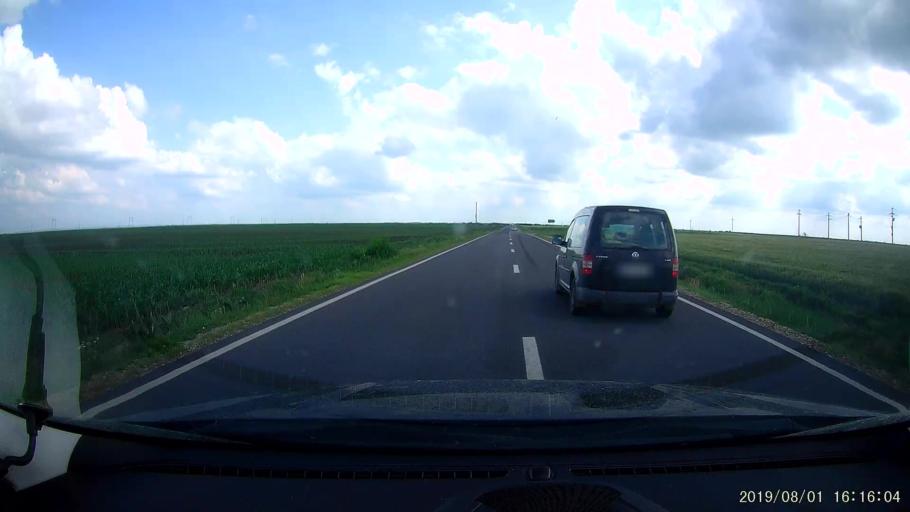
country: RO
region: Calarasi
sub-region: Comuna Stefan Voda
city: Stefan Voda
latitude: 44.3271
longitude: 27.3592
